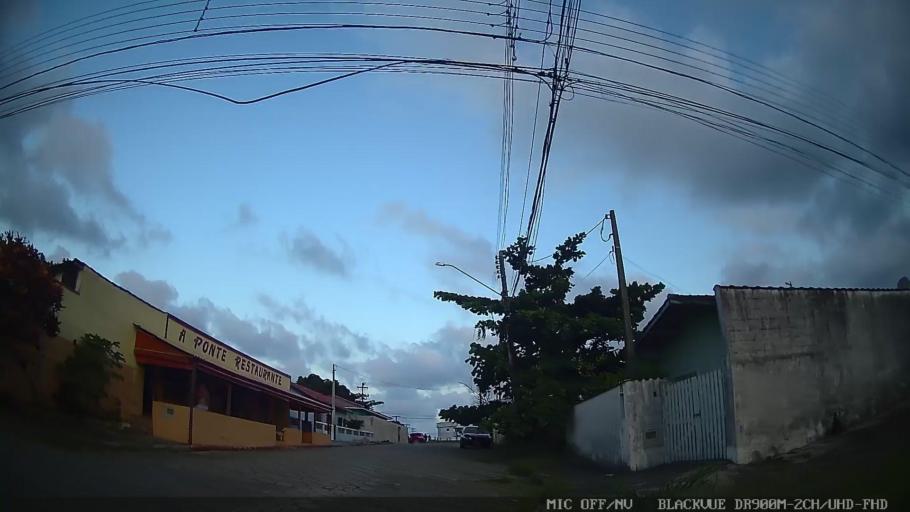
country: BR
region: Sao Paulo
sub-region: Peruibe
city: Peruibe
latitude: -24.3268
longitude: -47.0038
